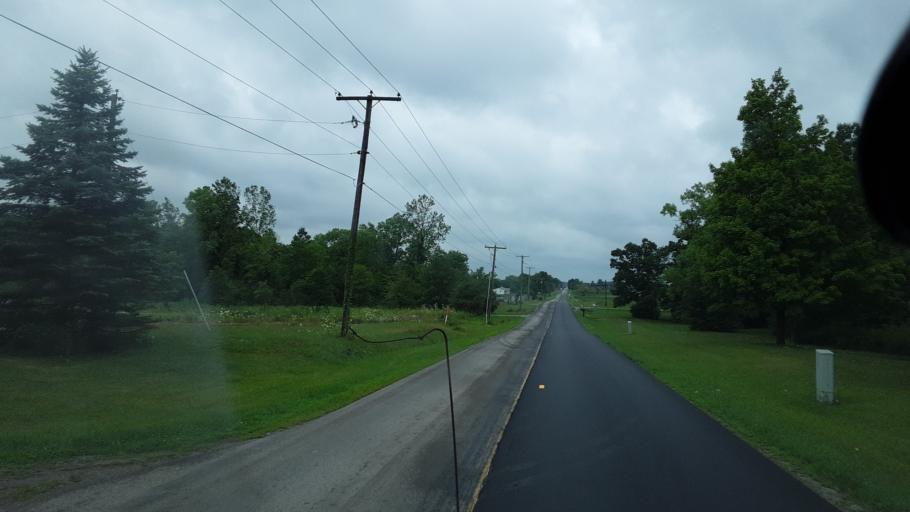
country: US
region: Indiana
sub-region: Allen County
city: New Haven
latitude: 40.9477
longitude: -85.0050
